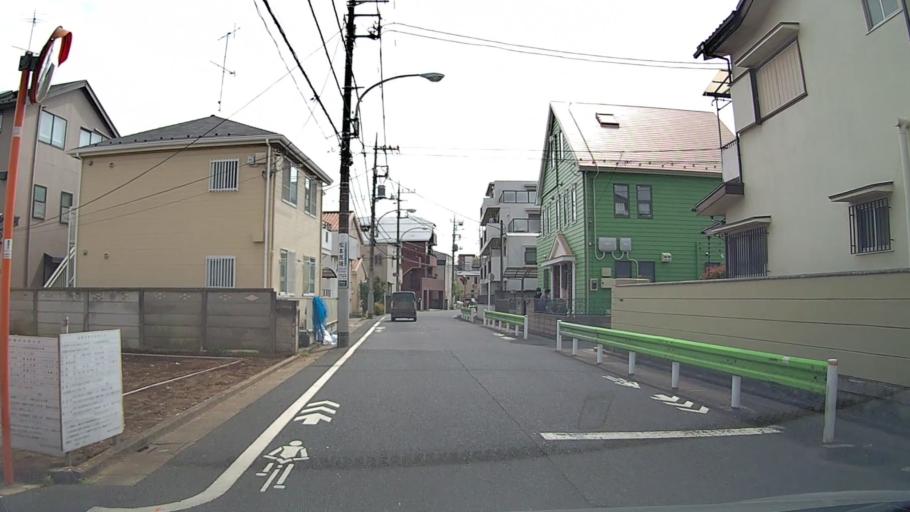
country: JP
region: Tokyo
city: Musashino
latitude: 35.7433
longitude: 139.5965
